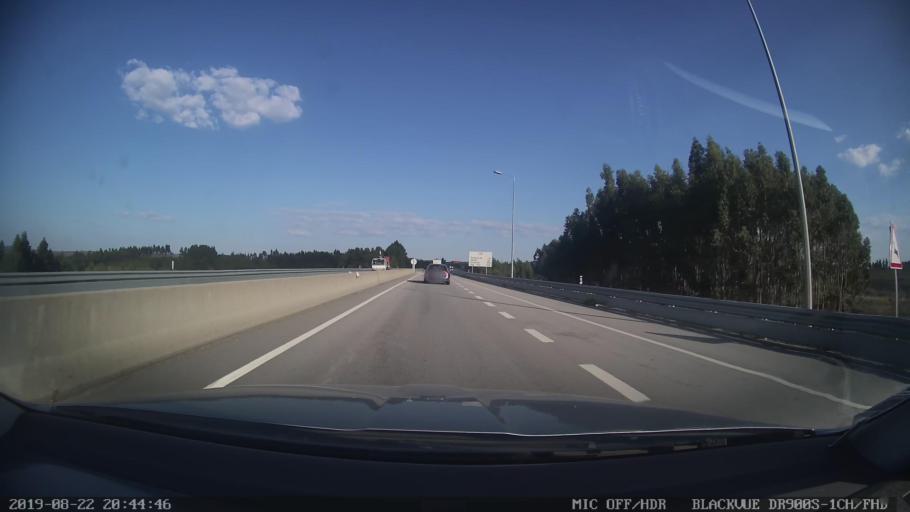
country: PT
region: Castelo Branco
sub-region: Proenca-A-Nova
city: Proenca-a-Nova
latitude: 39.7098
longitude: -7.8574
